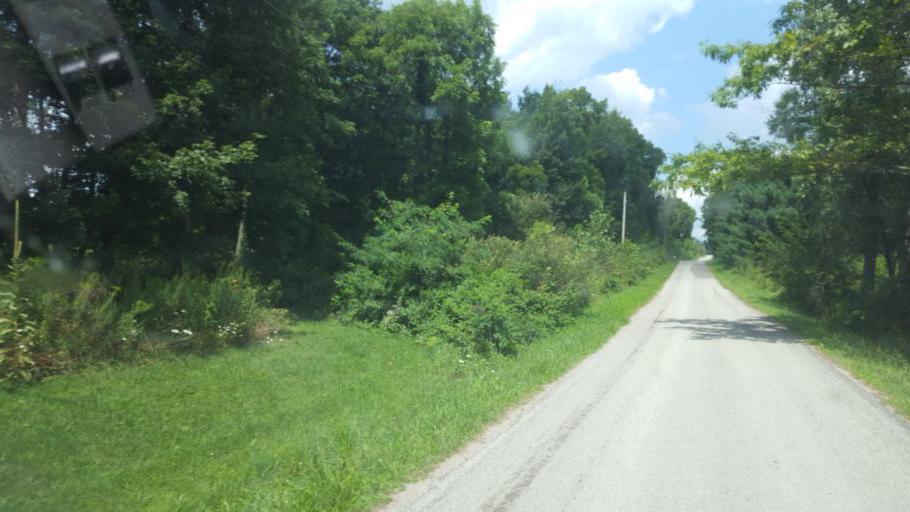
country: US
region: Ohio
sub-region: Knox County
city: Centerburg
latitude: 40.3553
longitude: -82.6357
